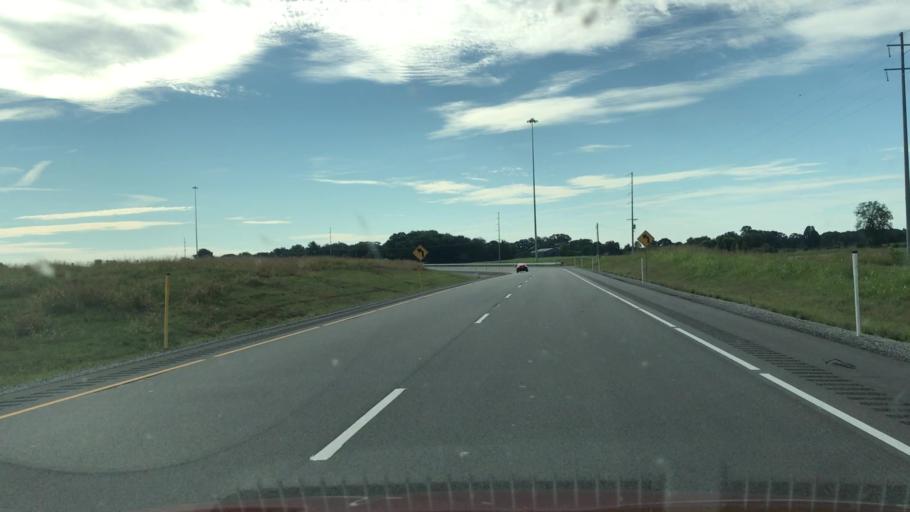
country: US
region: Kentucky
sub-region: Warren County
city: Bowling Green
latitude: 37.0097
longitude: -86.3330
